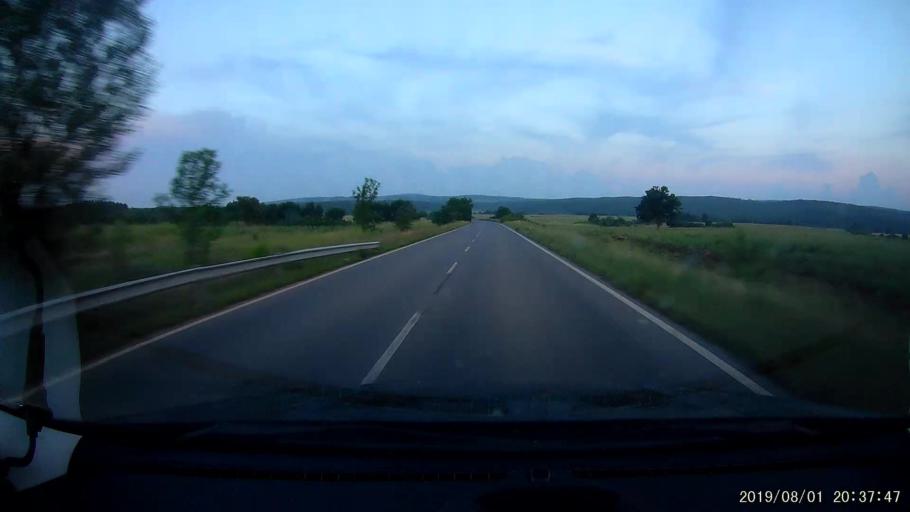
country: BG
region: Yambol
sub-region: Obshtina Elkhovo
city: Elkhovo
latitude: 42.0404
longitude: 26.5957
